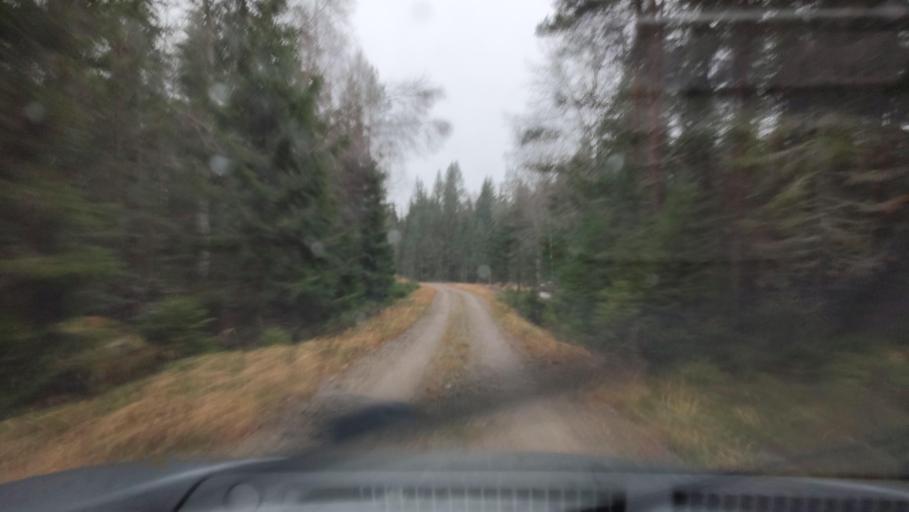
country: FI
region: Southern Ostrobothnia
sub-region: Suupohja
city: Karijoki
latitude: 62.1802
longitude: 21.7307
